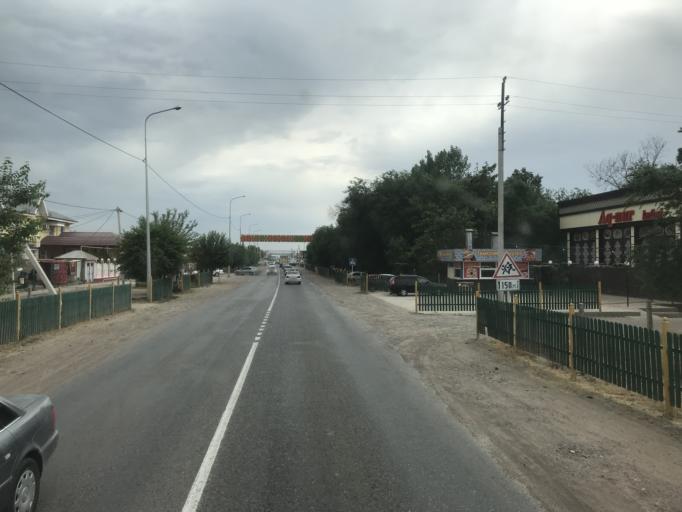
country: KZ
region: Ongtustik Qazaqstan
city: Saryaghash
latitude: 41.3431
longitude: 68.9546
